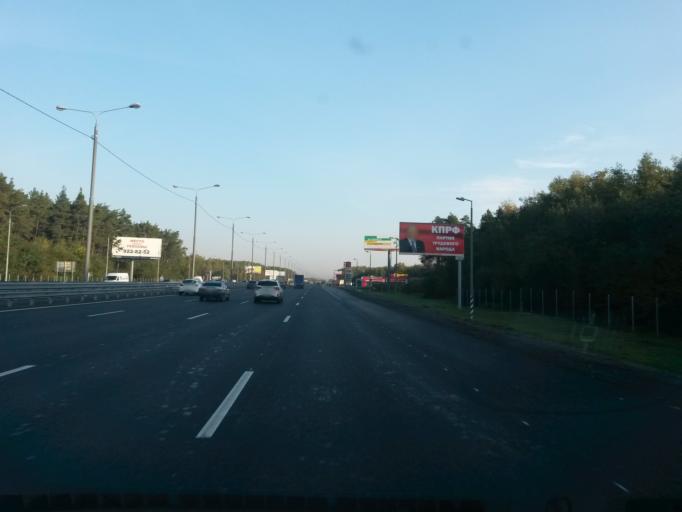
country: RU
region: Moskovskaya
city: Shcherbinka
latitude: 55.4891
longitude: 37.6126
